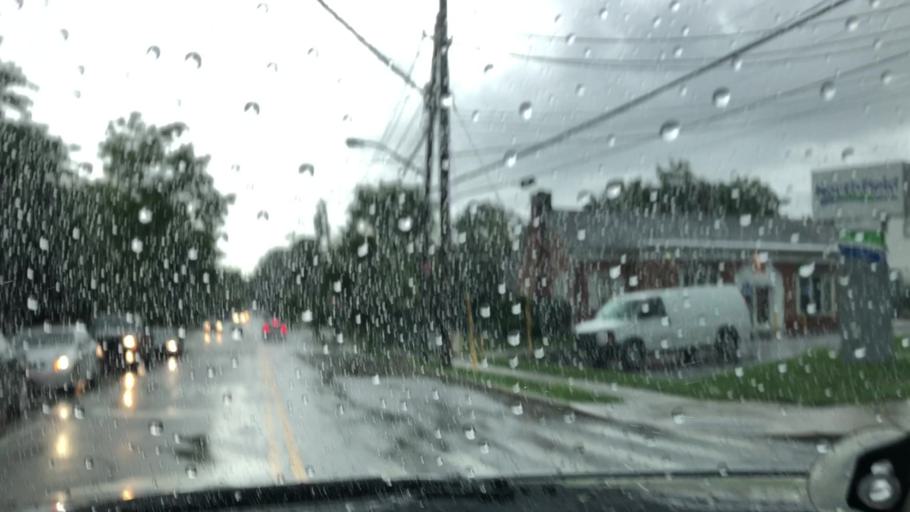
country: US
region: New Jersey
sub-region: Middlesex County
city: Carteret
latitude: 40.5269
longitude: -74.2013
